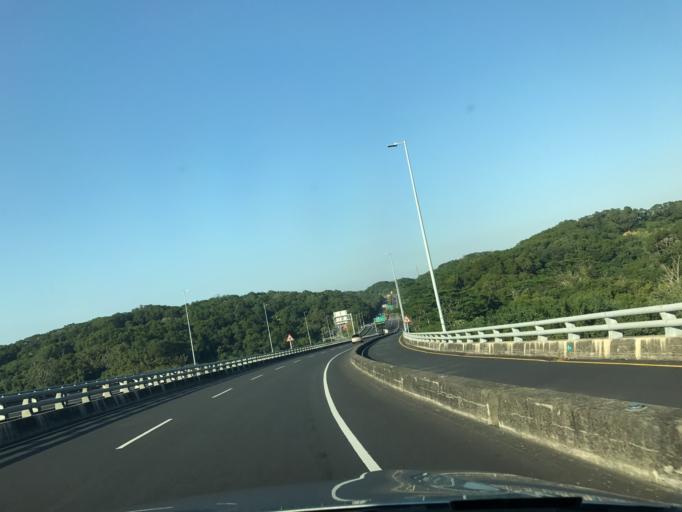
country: TW
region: Taiwan
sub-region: Hsinchu
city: Hsinchu
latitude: 24.7706
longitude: 120.9523
